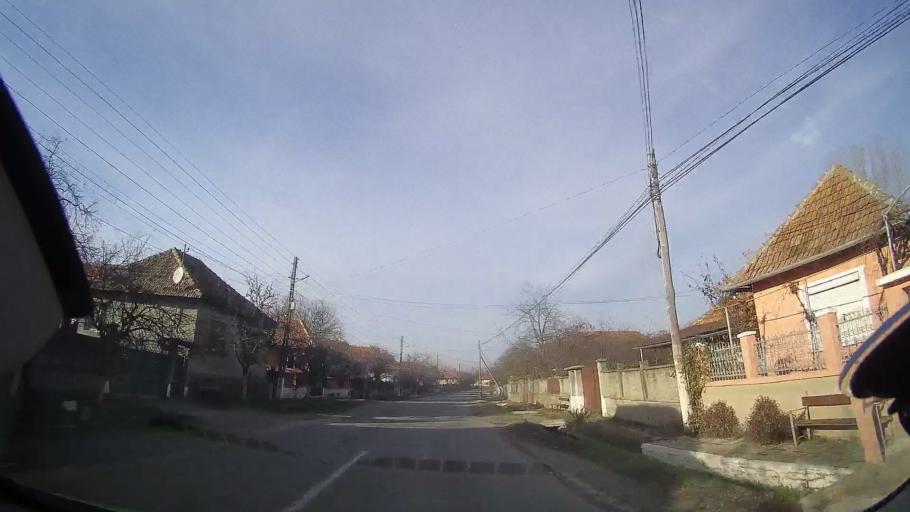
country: RO
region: Bihor
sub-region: Comuna Brusturi
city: Brusturi
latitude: 47.1456
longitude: 22.2574
